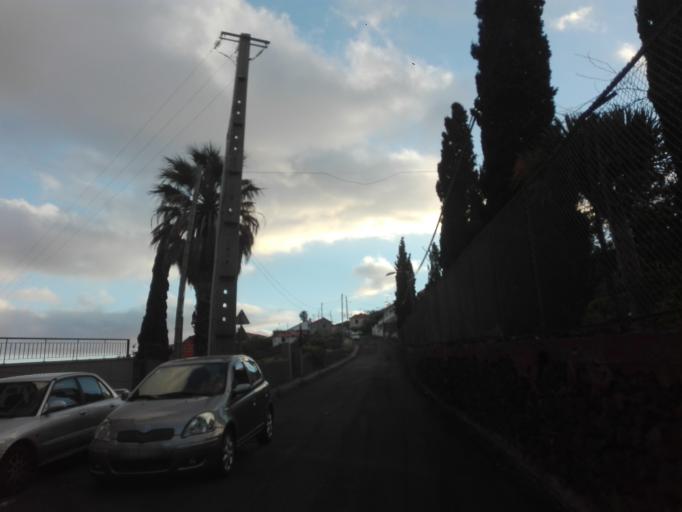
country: PT
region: Madeira
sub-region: Santa Cruz
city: Camacha
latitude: 32.6556
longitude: -16.8298
